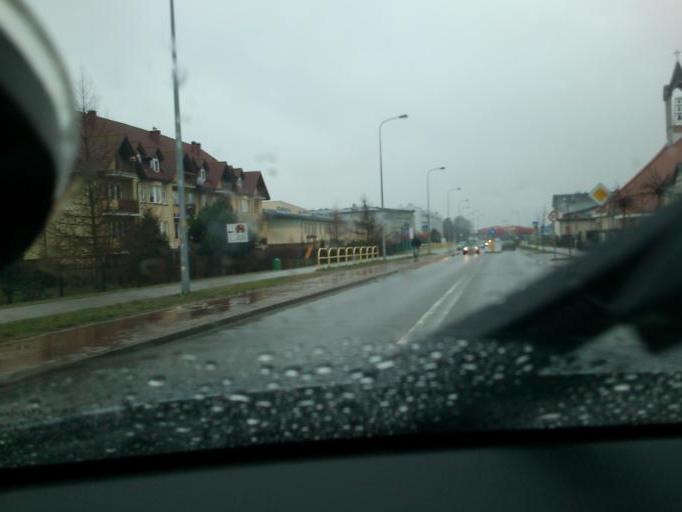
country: PL
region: Pomeranian Voivodeship
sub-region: Gdynia
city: Wielki Kack
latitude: 54.4226
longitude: 18.4786
